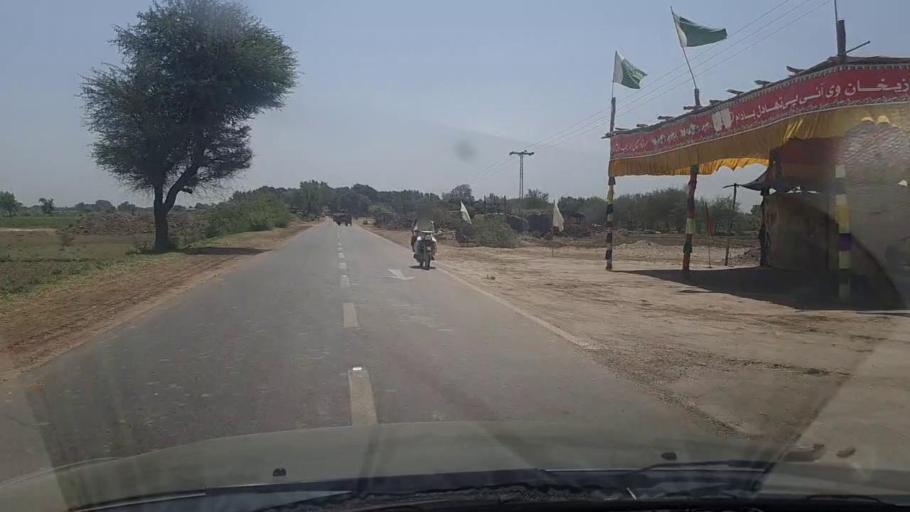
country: PK
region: Sindh
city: Tando Jam
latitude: 25.3143
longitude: 68.5645
